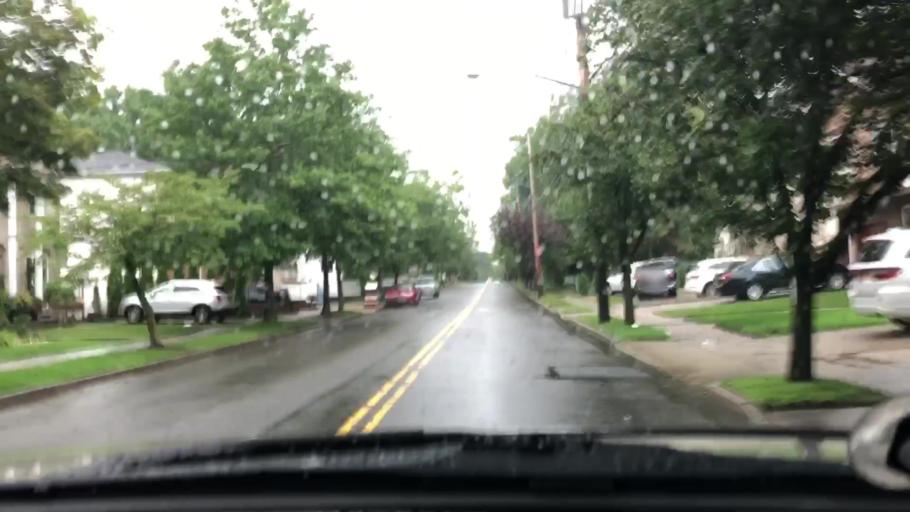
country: US
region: New York
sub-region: Richmond County
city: Staten Island
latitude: 40.5280
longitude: -74.1889
